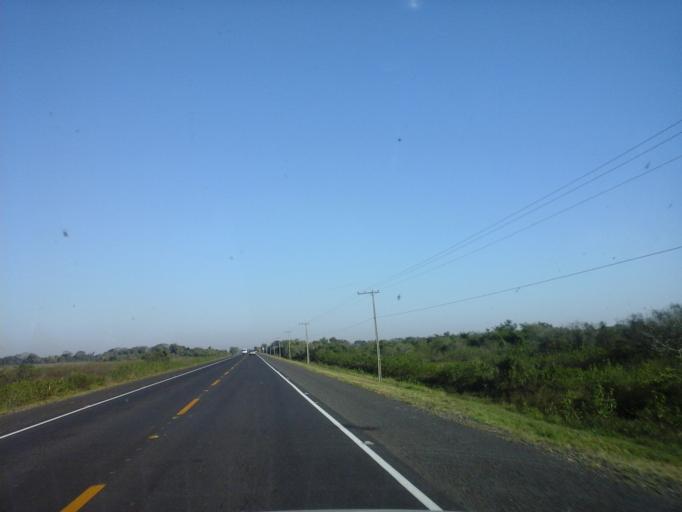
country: PY
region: Neembucu
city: Pilar
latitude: -26.8557
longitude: -58.1957
